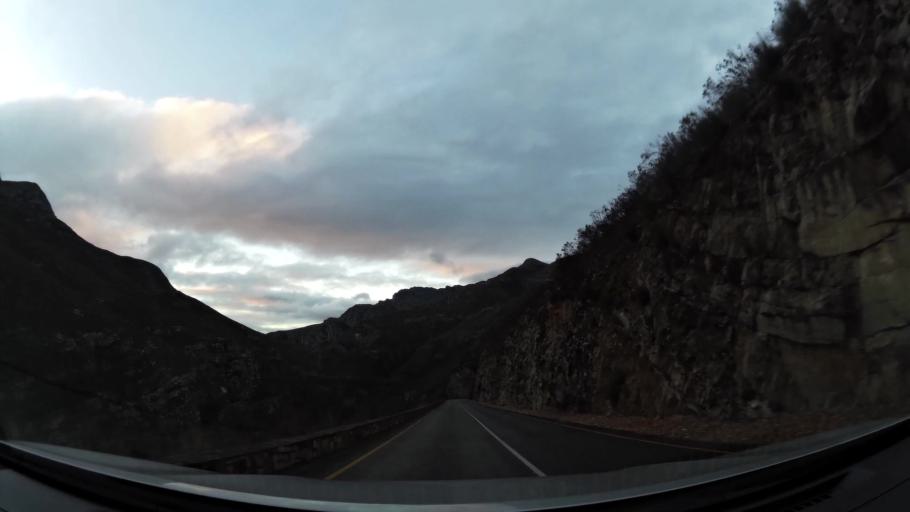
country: ZA
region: Western Cape
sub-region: Overberg District Municipality
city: Swellendam
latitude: -33.9736
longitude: 20.6996
